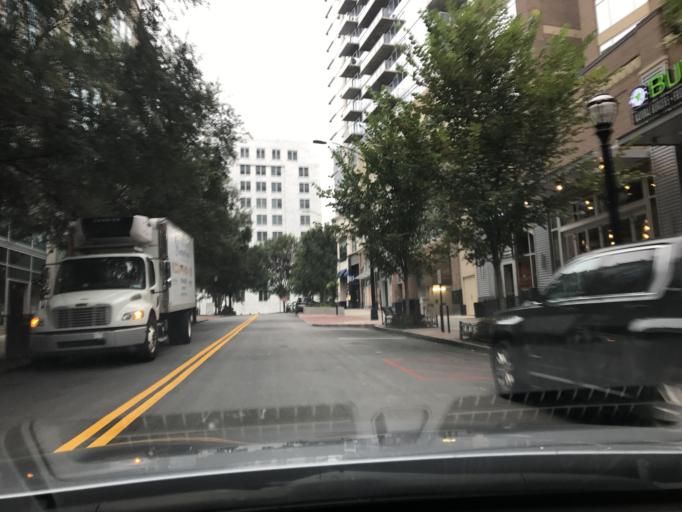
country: US
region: Georgia
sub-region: Fulton County
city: Atlanta
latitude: 33.7843
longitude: -84.3844
